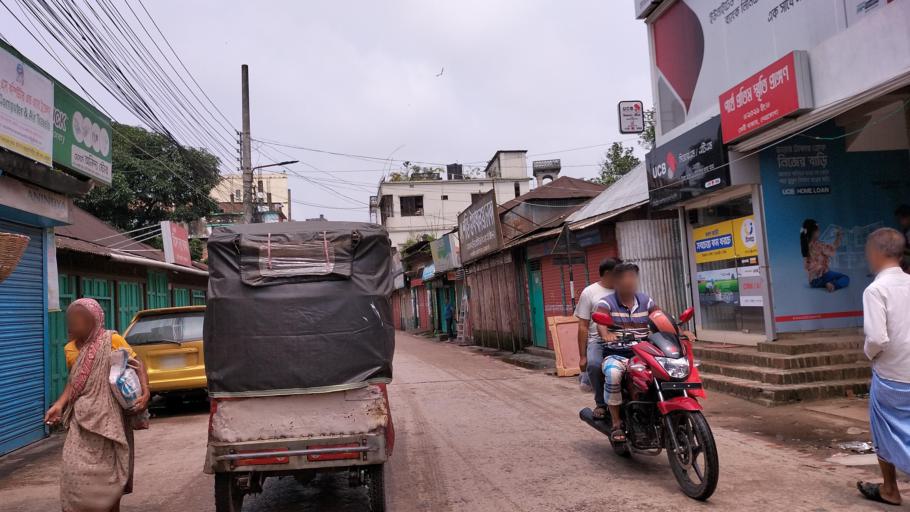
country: BD
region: Dhaka
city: Netrakona
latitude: 24.8849
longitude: 90.7325
